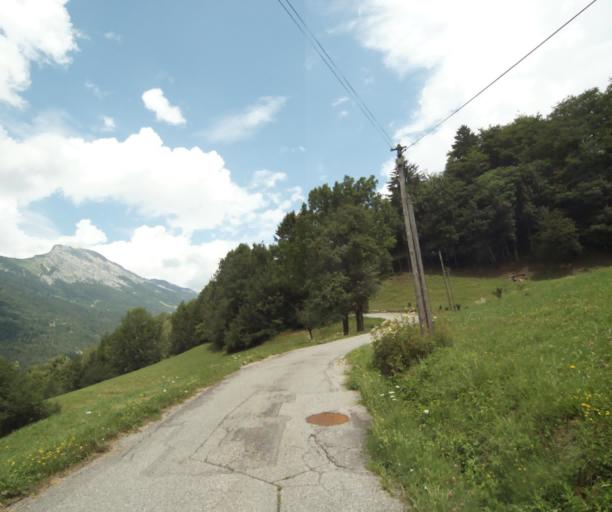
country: FR
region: Rhone-Alpes
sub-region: Departement de la Haute-Savoie
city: Thones
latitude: 45.8864
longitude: 6.3409
